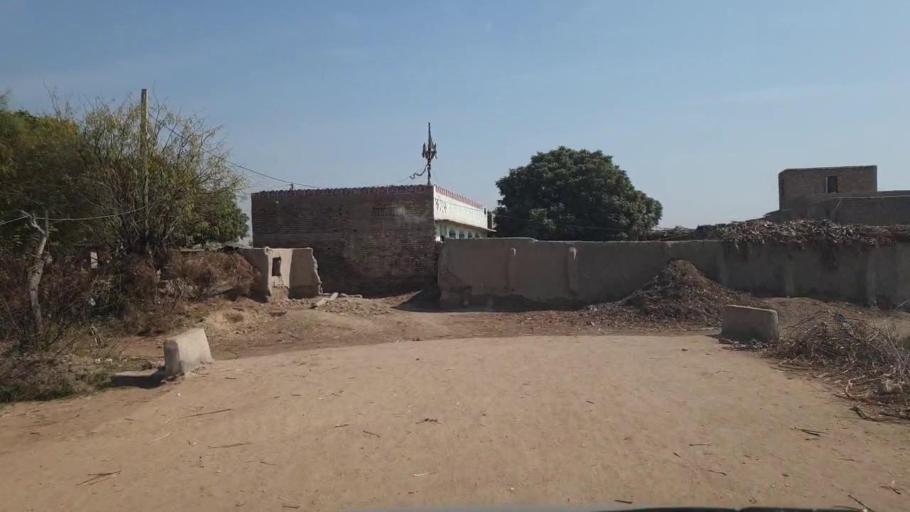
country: PK
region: Sindh
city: Chambar
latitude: 25.3712
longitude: 68.8187
